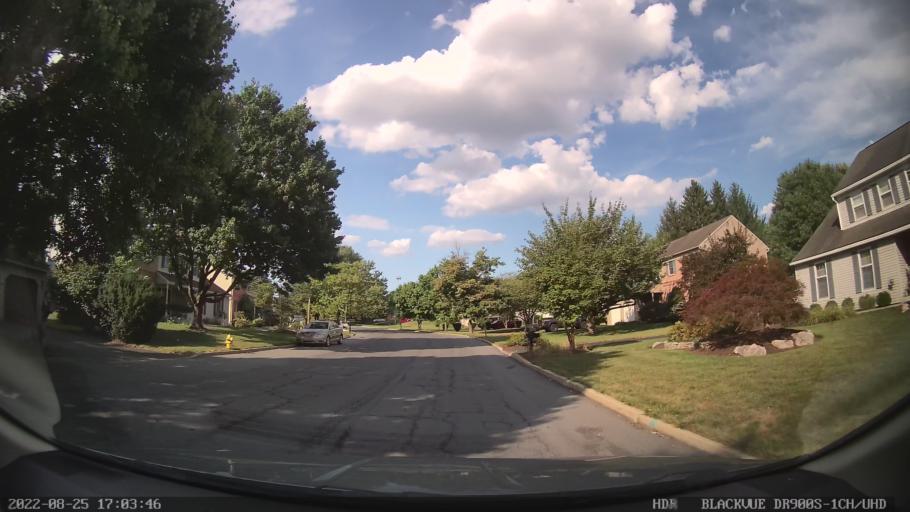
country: US
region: Pennsylvania
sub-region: Lehigh County
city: Emmaus
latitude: 40.5503
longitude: -75.4951
